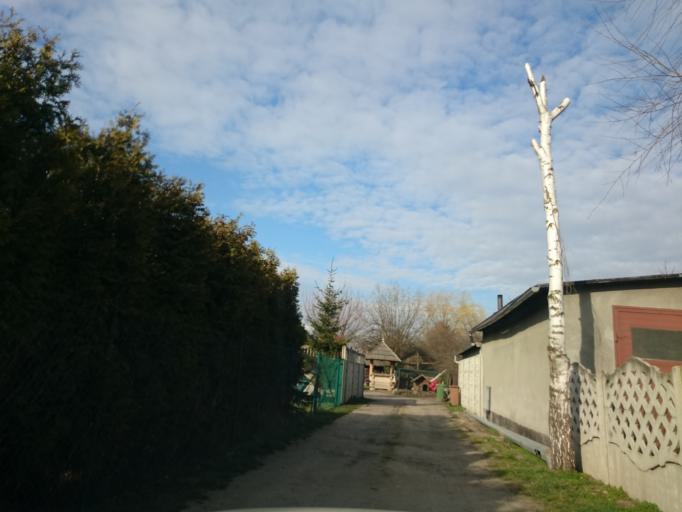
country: PL
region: Kujawsko-Pomorskie
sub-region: Powiat torunski
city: Lubicz Gorny
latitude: 53.0318
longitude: 18.7818
